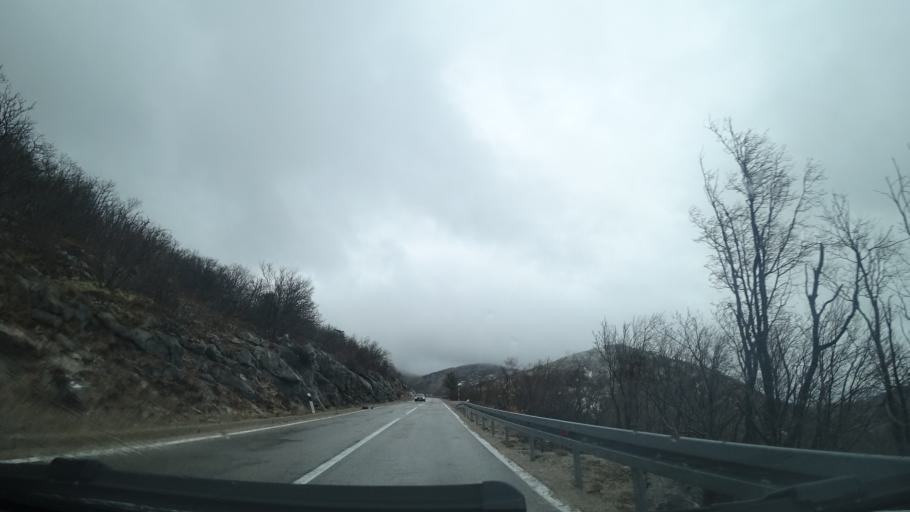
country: HR
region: Licko-Senjska
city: Karlobag
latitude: 44.5288
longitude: 15.1301
